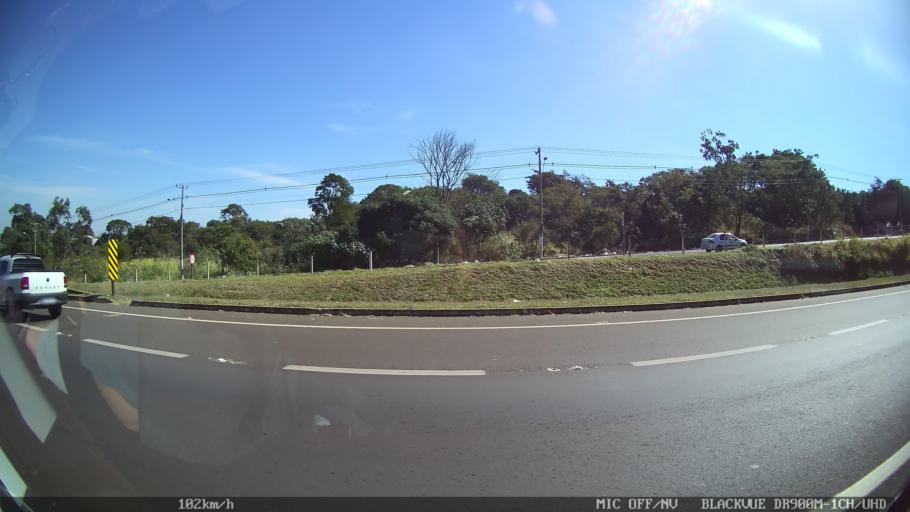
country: BR
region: Sao Paulo
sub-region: Franca
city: Franca
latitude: -20.5066
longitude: -47.4107
